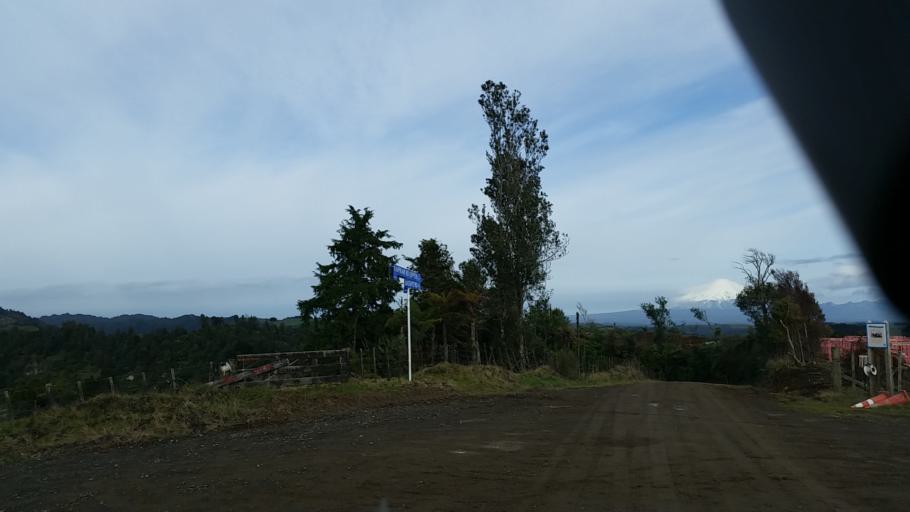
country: NZ
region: Taranaki
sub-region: New Plymouth District
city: Waitara
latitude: -39.0406
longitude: 174.4142
